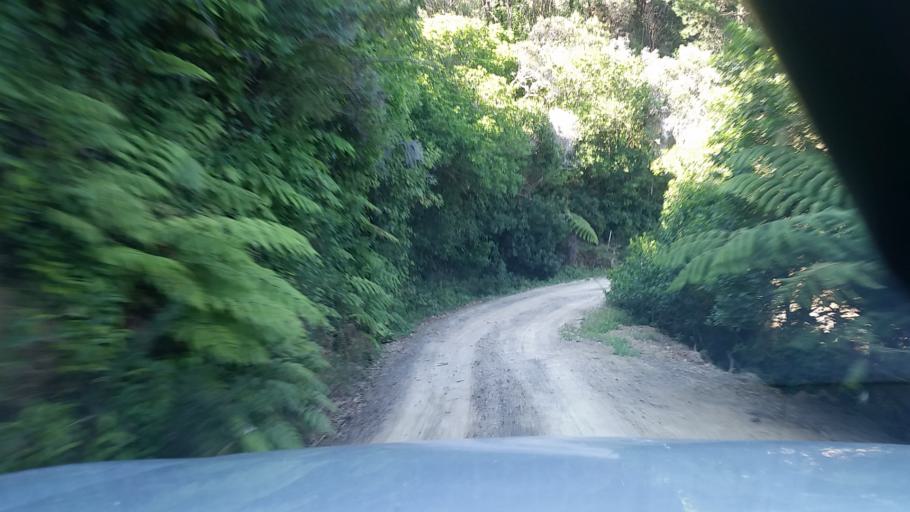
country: NZ
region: Marlborough
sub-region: Marlborough District
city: Picton
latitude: -41.3068
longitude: 174.1736
